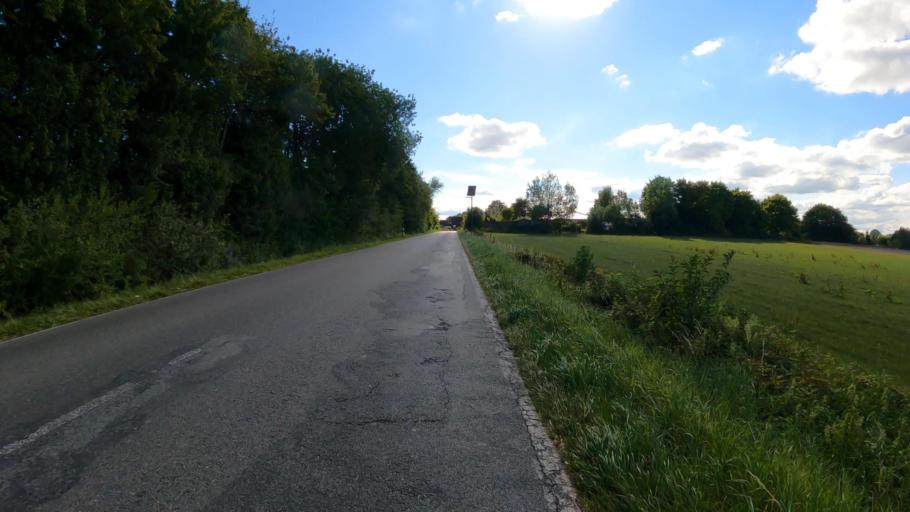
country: DE
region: Schleswig-Holstein
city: Stubben
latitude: 53.7210
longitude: 10.4113
